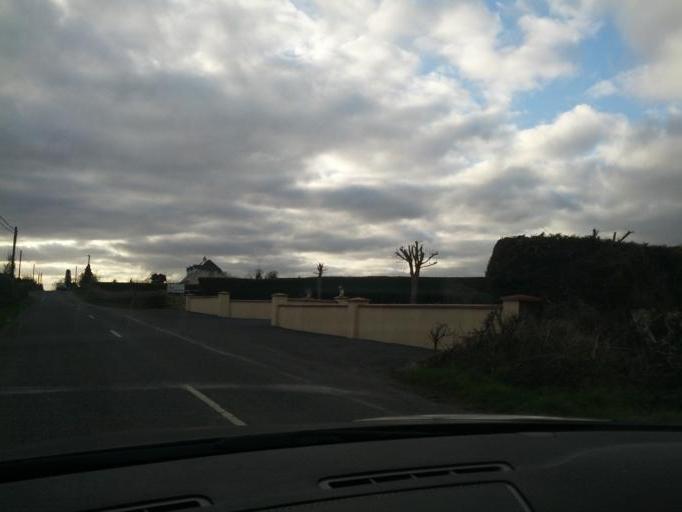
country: IE
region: Leinster
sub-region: Uibh Fhaili
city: Ferbane
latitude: 53.3236
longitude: -7.9043
